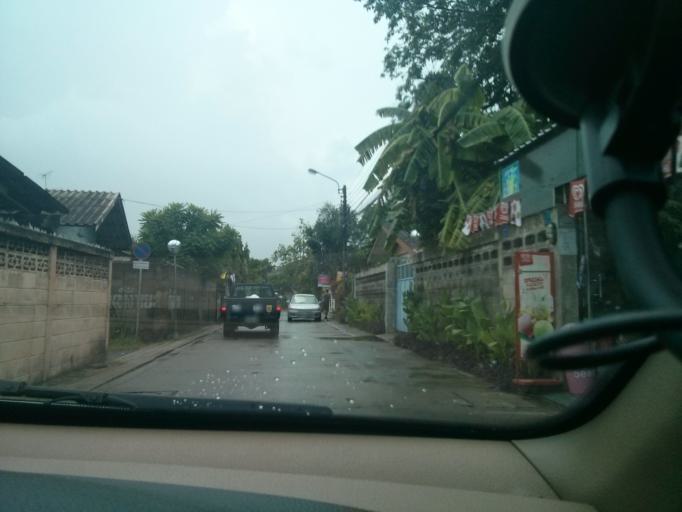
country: TH
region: Nonthaburi
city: Mueang Nonthaburi
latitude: 13.8412
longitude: 100.5155
